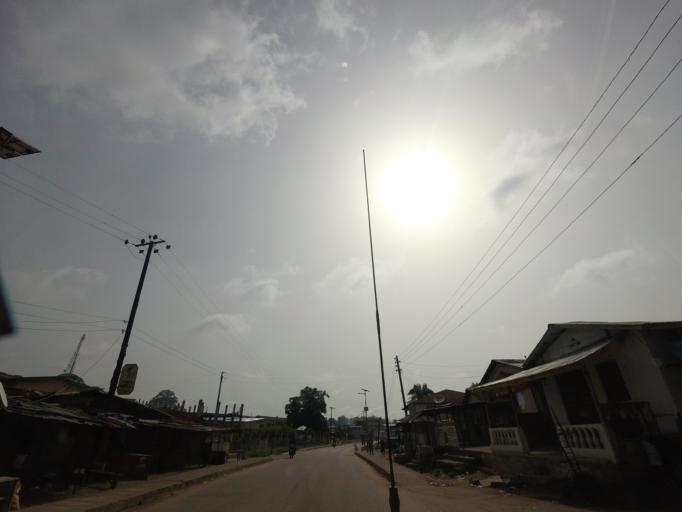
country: SL
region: Southern Province
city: Bo
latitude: 7.9587
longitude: -11.7419
